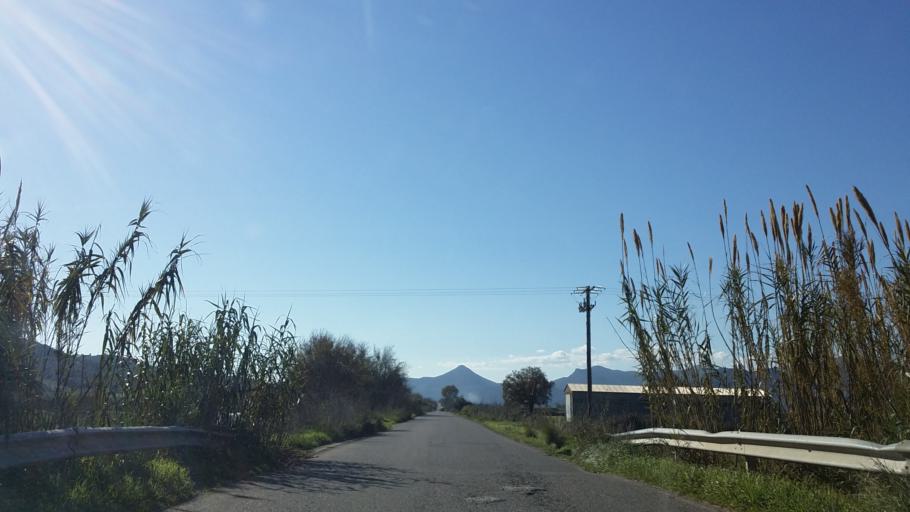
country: GR
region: West Greece
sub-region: Nomos Aitolias kai Akarnanias
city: Vonitsa
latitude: 38.8663
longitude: 20.8828
